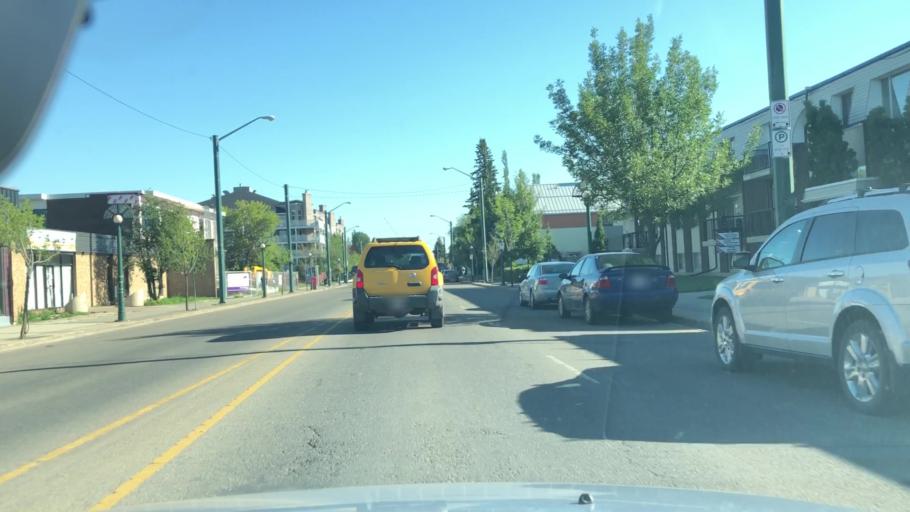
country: CA
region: Alberta
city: Edmonton
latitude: 53.5570
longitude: -113.5360
